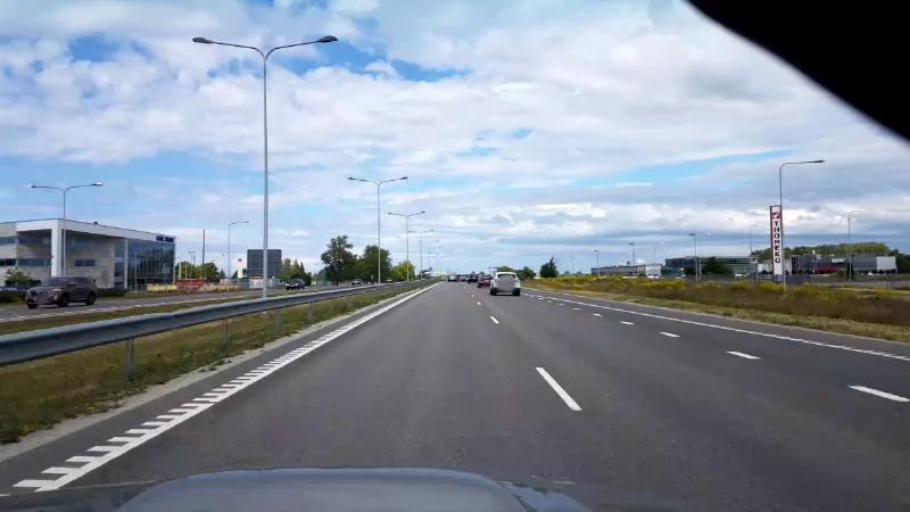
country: EE
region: Harju
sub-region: Saue vald
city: Laagri
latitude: 59.3444
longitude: 24.6201
